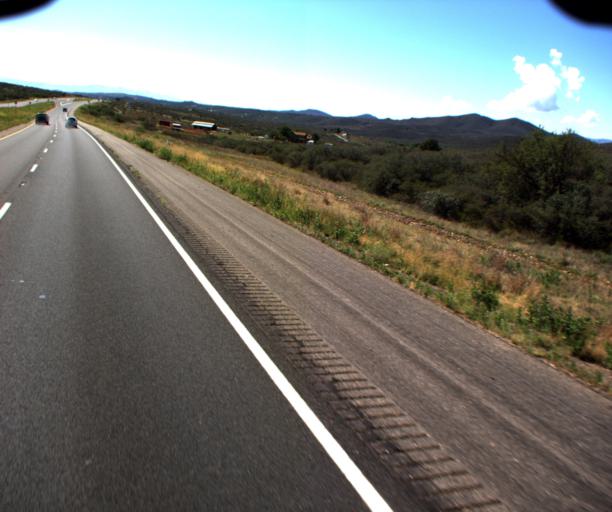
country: US
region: Arizona
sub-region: Yavapai County
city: Mayer
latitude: 34.4330
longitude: -112.2591
